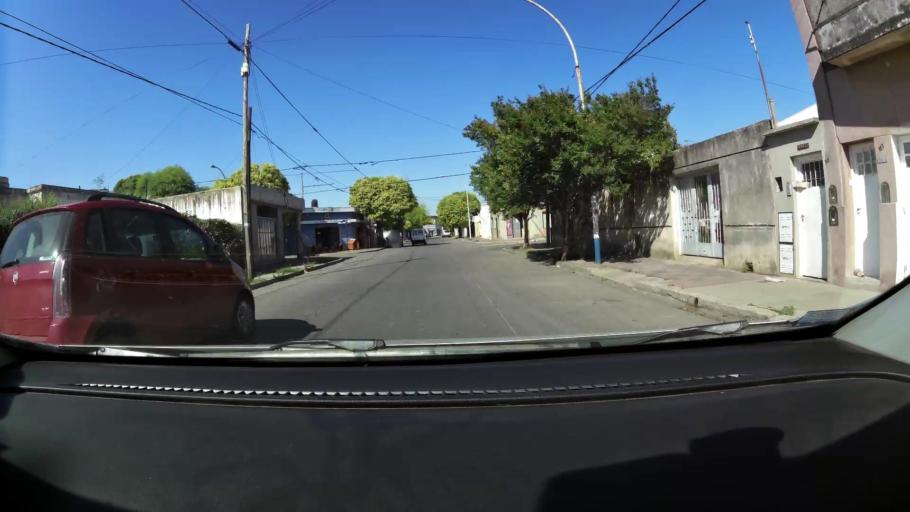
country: AR
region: Cordoba
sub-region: Departamento de Capital
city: Cordoba
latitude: -31.4388
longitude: -64.1604
